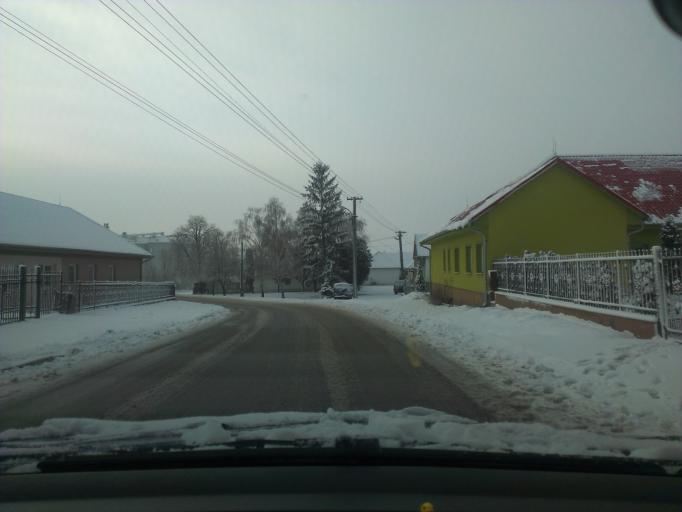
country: SK
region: Trnavsky
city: Hlohovec
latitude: 48.4748
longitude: 17.9884
